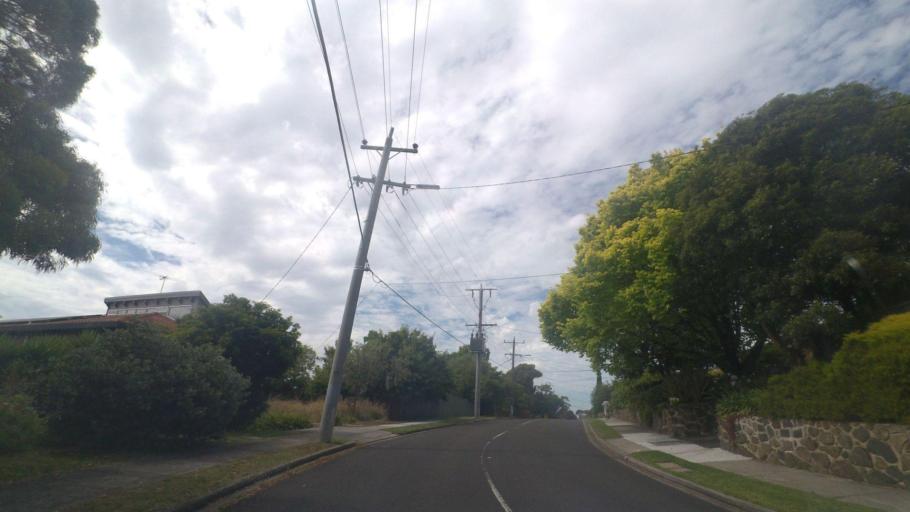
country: AU
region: Victoria
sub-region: Banyule
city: Viewbank
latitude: -37.7429
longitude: 145.0904
